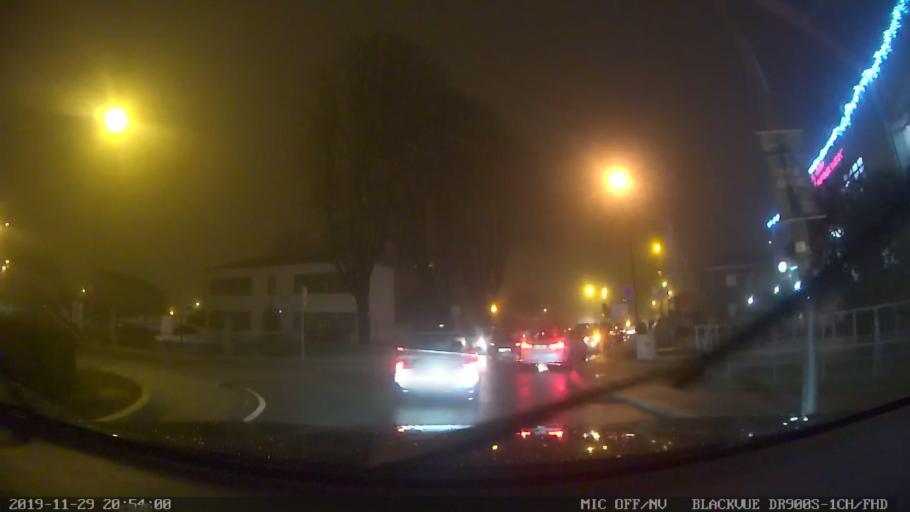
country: PT
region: Porto
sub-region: Matosinhos
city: Senhora da Hora
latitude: 41.1913
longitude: -8.6528
